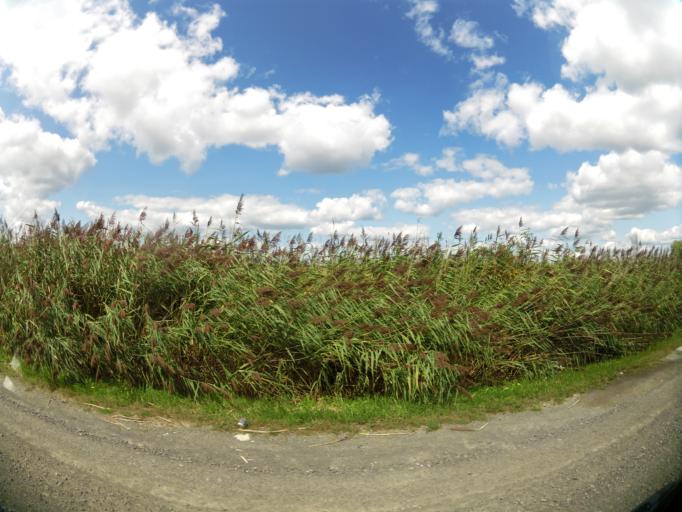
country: CA
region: Ontario
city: Ottawa
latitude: 45.4382
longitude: -75.4970
